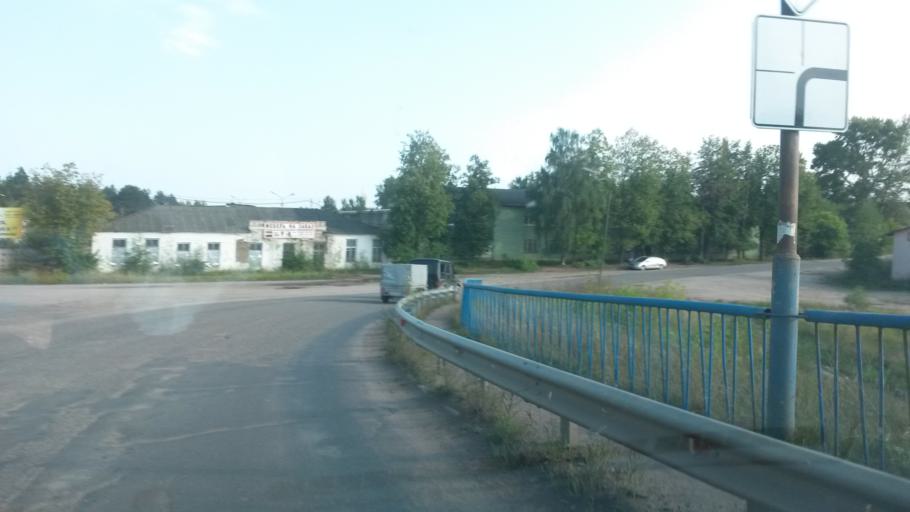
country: RU
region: Jaroslavl
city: Petrovsk
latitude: 57.0033
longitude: 39.2752
